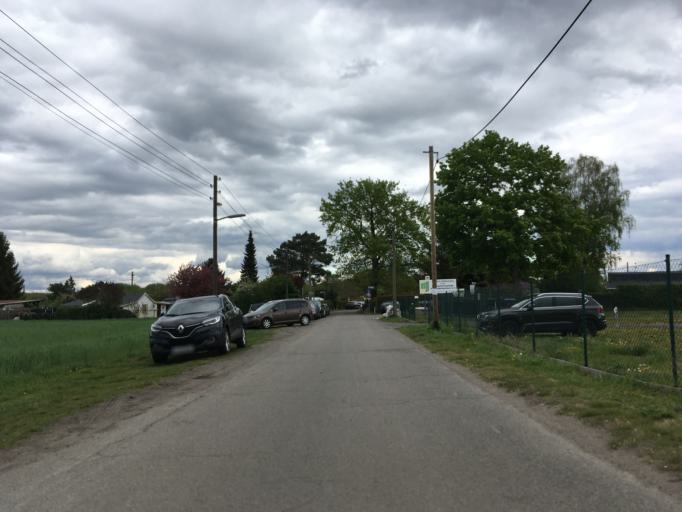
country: DE
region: Berlin
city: Blankenfelde
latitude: 52.6183
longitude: 13.4110
